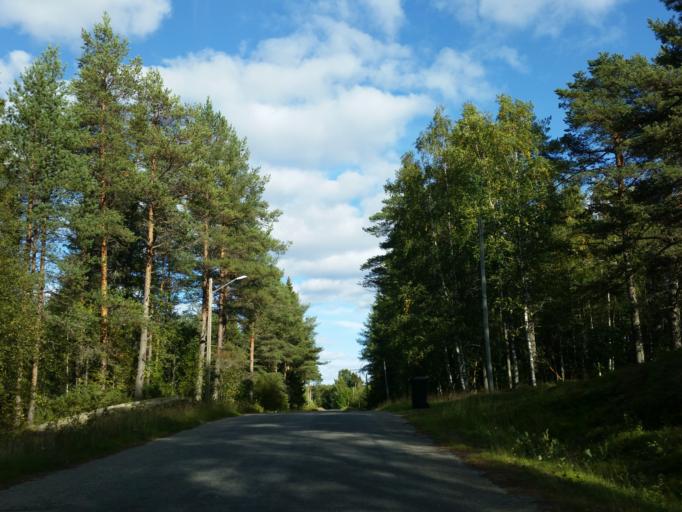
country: SE
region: Vaesterbotten
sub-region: Robertsfors Kommun
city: Robertsfors
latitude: 64.1727
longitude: 20.9499
